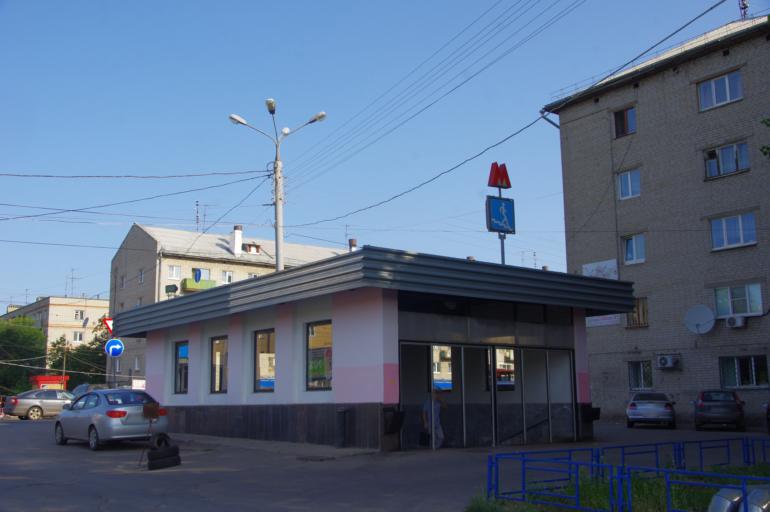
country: RU
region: Nizjnij Novgorod
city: Nizhniy Novgorod
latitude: 56.2978
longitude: 43.9381
